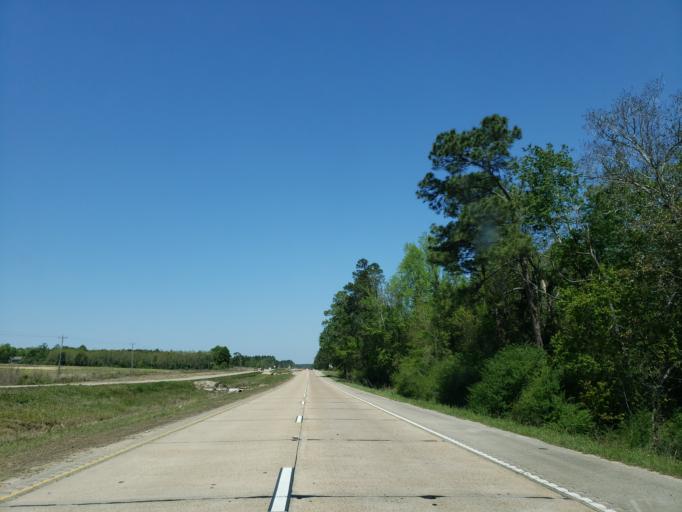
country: US
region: Mississippi
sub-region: Lamar County
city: Purvis
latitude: 31.0740
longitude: -89.2097
